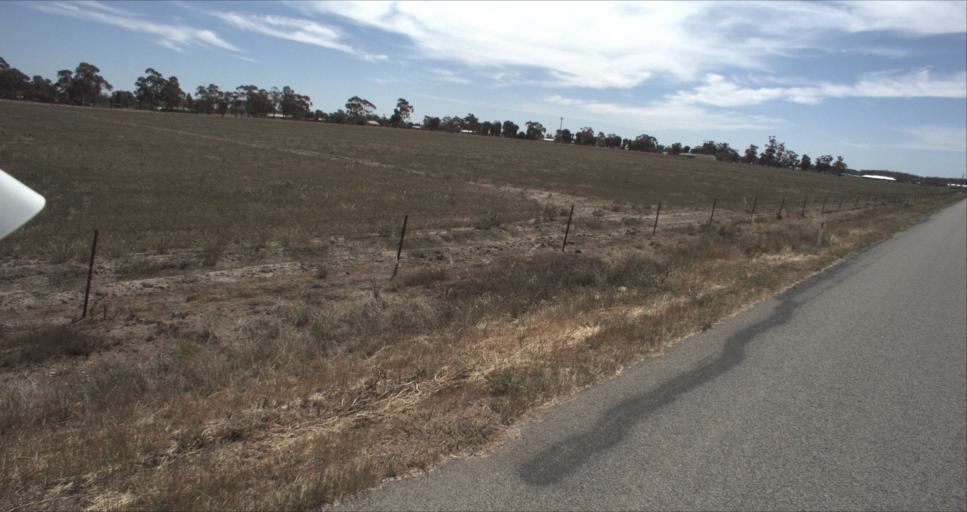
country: AU
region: New South Wales
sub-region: Leeton
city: Leeton
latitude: -34.5989
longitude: 146.4160
